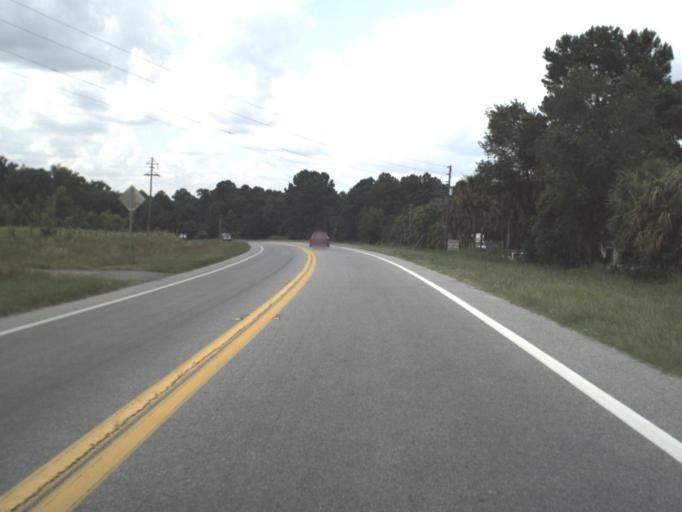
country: US
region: Florida
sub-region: Hamilton County
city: Jasper
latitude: 30.4926
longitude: -82.9310
